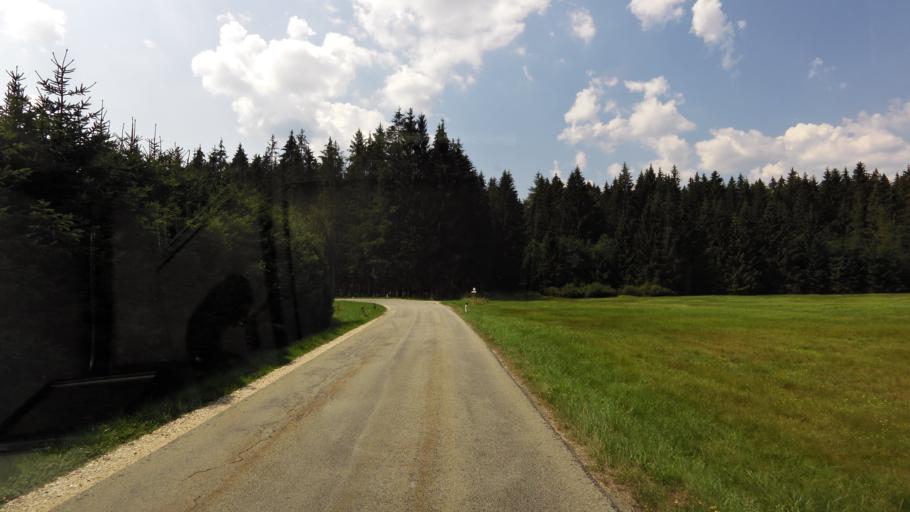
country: AT
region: Upper Austria
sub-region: Politischer Bezirk Vocklabruck
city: Fornach
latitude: 48.0598
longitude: 13.4116
